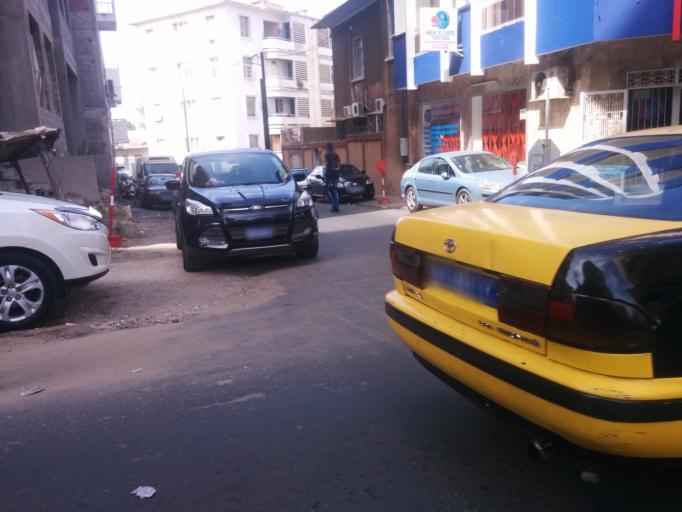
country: SN
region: Dakar
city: Dakar
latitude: 14.6724
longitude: -17.4336
